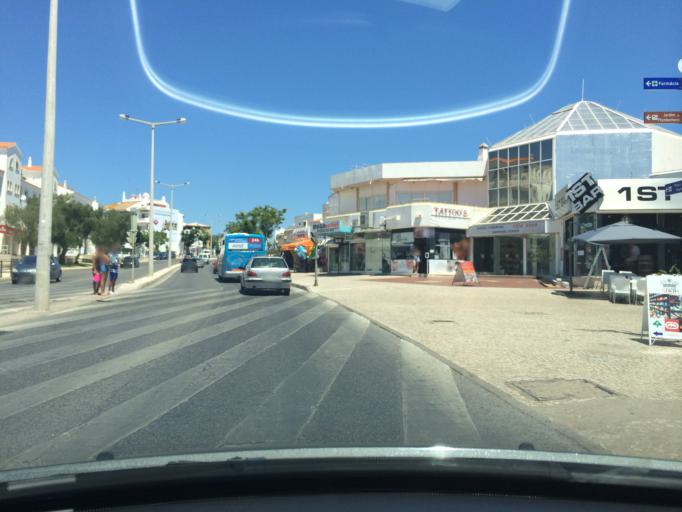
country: PT
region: Faro
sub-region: Albufeira
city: Albufeira
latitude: 37.0943
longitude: -8.2284
